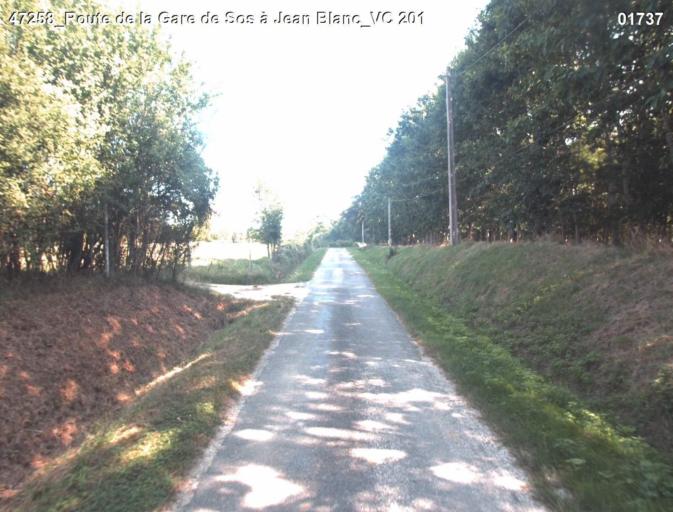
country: FR
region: Midi-Pyrenees
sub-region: Departement du Gers
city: Montreal
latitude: 44.0321
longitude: 0.1560
